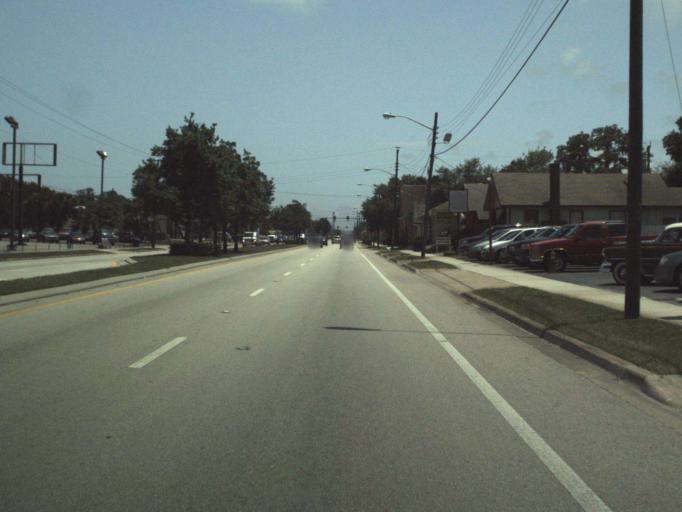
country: US
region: Florida
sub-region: Volusia County
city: Holly Hill
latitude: 29.2312
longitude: -81.0338
